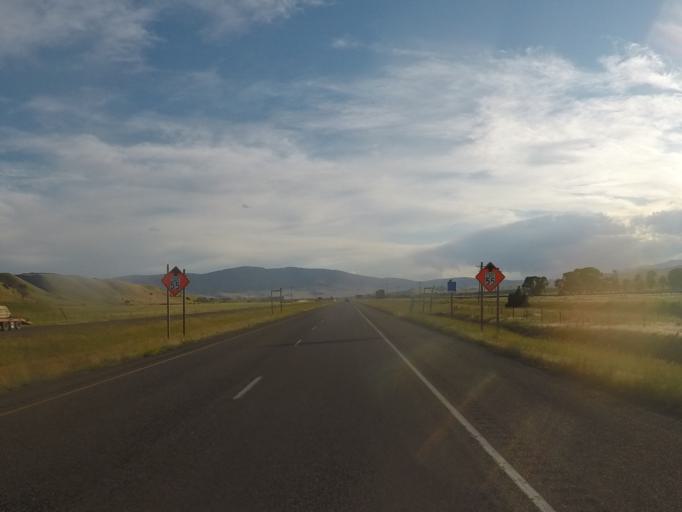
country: US
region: Montana
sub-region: Park County
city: Livingston
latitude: 45.6970
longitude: -110.4799
